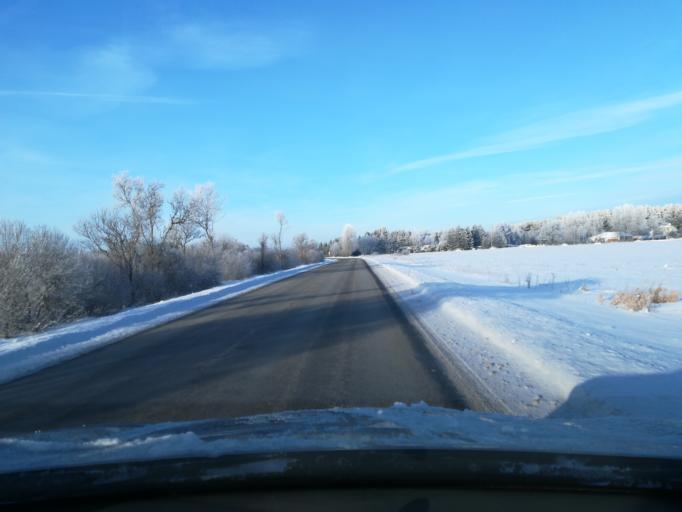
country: EE
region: Harju
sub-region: Harku vald
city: Tabasalu
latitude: 59.3714
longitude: 24.4748
